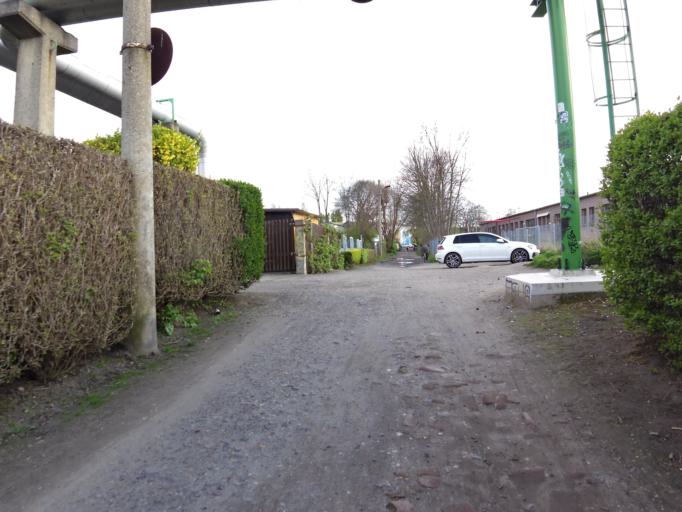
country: DE
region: Saxony
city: Leipzig
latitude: 51.3118
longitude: 12.3827
